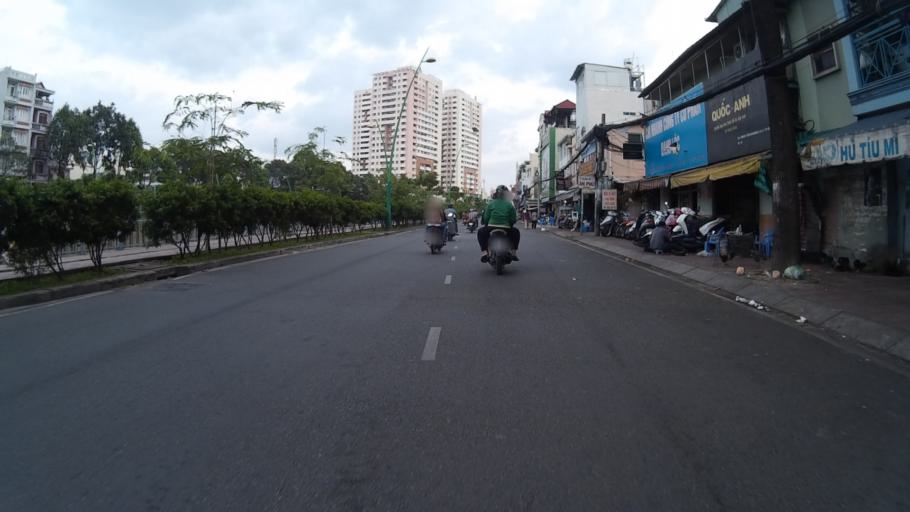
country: VN
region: Ho Chi Minh City
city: Quan Phu Nhuan
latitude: 10.7870
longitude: 106.6727
